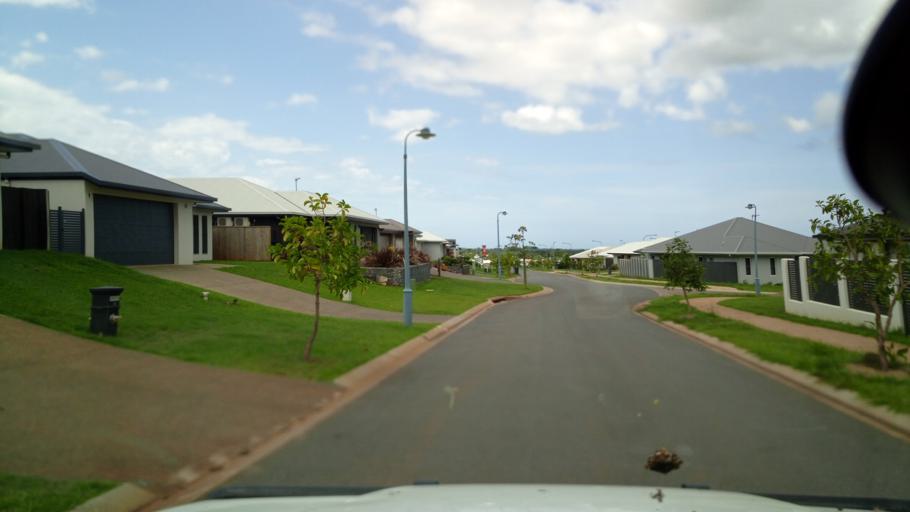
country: AU
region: Queensland
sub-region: Cairns
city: Redlynch
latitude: -16.8974
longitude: 145.6932
